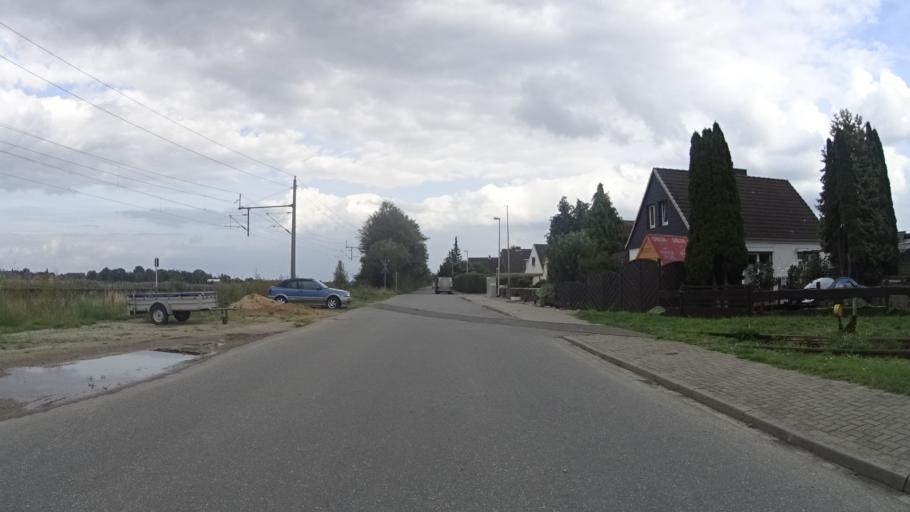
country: DE
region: Schleswig-Holstein
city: Gluckstadt
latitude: 53.7840
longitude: 9.4374
